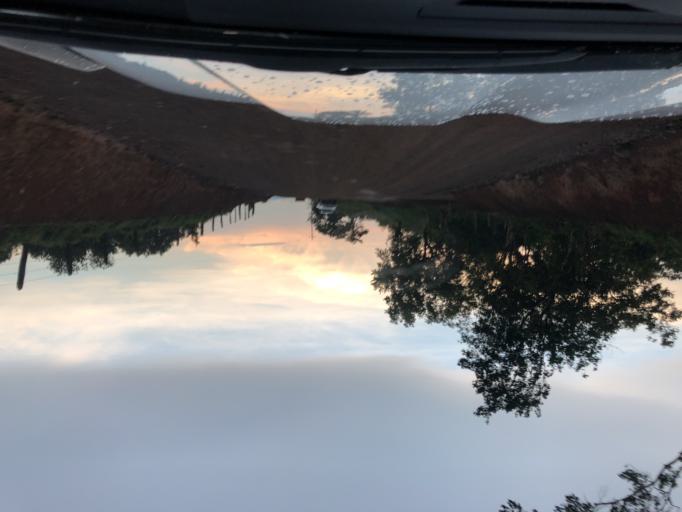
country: NI
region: Chontales
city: La Libertad
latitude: 12.1929
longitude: -85.1766
